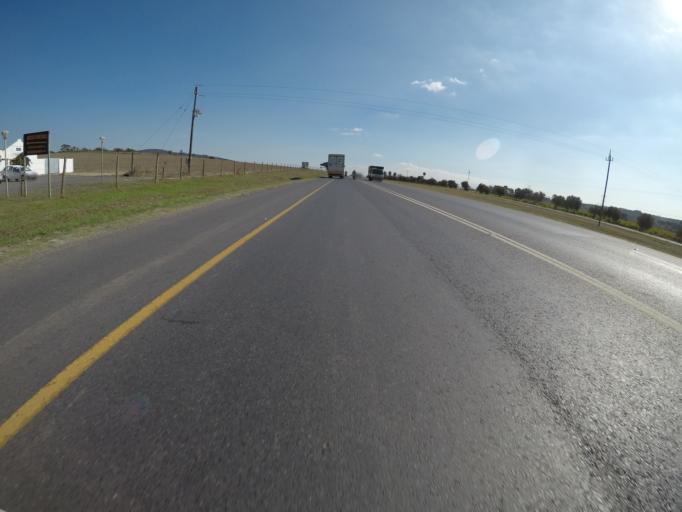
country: ZA
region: Western Cape
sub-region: City of Cape Town
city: Kraaifontein
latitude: -33.8909
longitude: 18.7412
